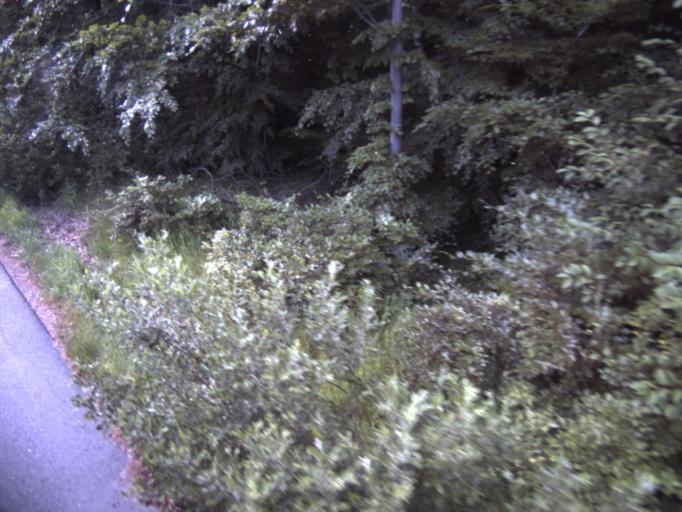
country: SE
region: Skane
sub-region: Helsingborg
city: Helsingborg
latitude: 56.0897
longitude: 12.6871
